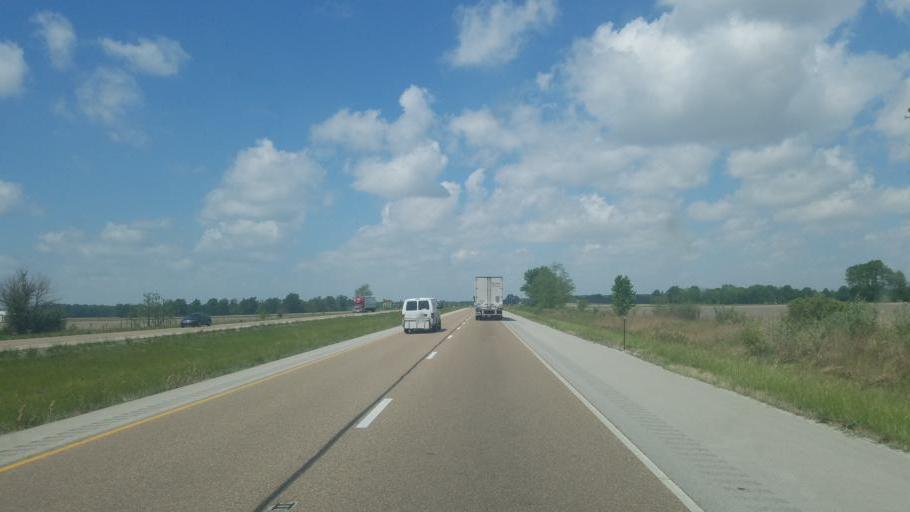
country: US
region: Illinois
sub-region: Cumberland County
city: Greenup
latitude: 39.2748
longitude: -88.0957
